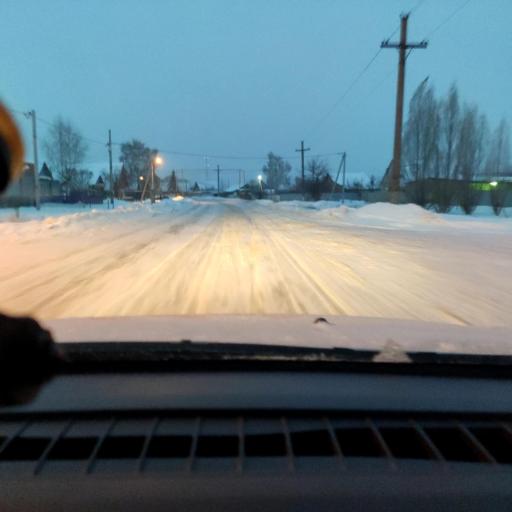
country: RU
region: Samara
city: Kinel'-Cherkassy
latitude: 53.4605
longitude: 51.5252
